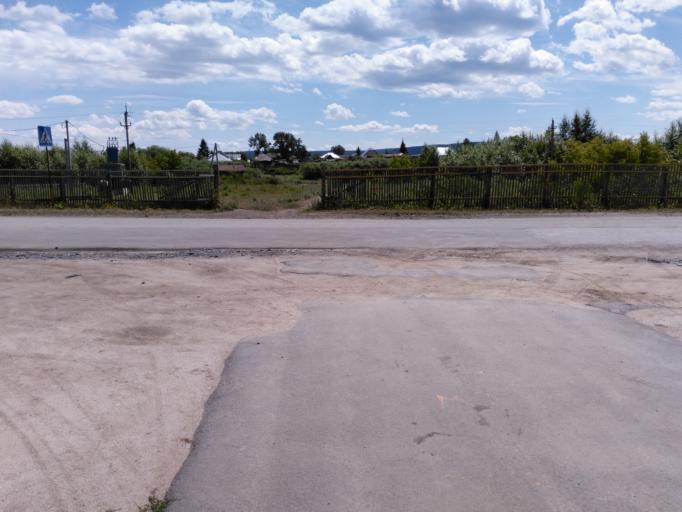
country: RU
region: Bashkortostan
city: Akhunovo
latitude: 54.2108
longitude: 59.5989
